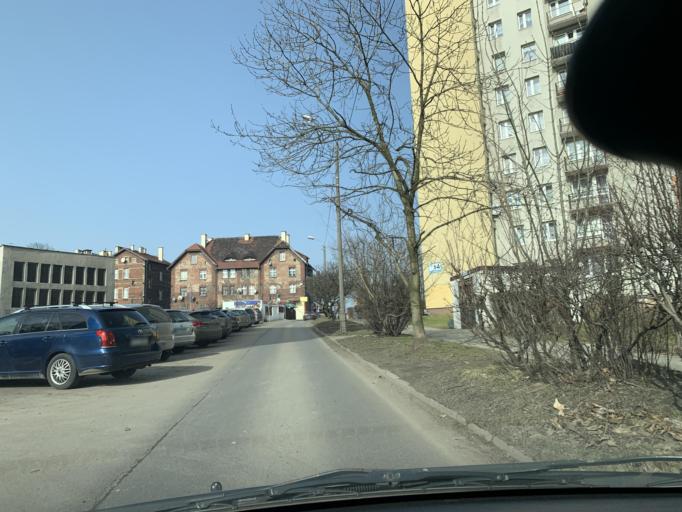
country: PL
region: Silesian Voivodeship
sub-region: Bytom
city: Bytom
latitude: 50.3365
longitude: 18.8867
